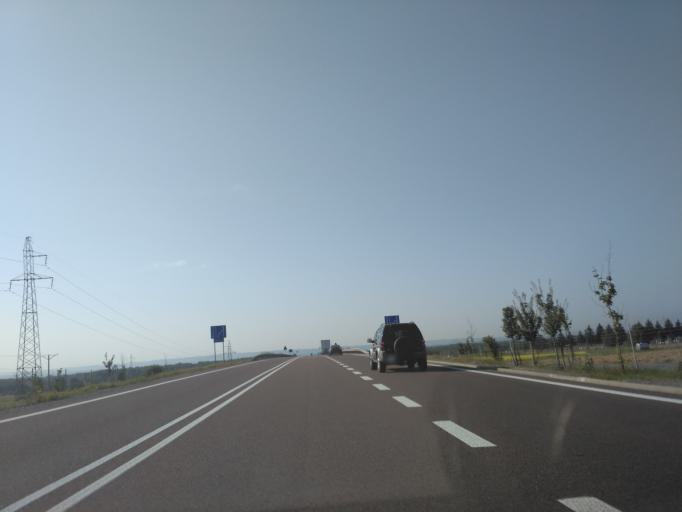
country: PL
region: Subcarpathian Voivodeship
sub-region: Powiat rzeszowski
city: Wolka Podlesna
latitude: 50.1416
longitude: 22.0788
